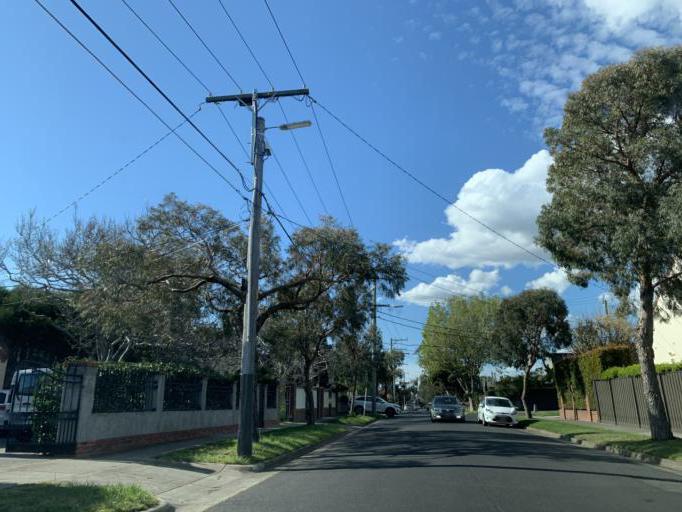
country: AU
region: Victoria
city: Hampton
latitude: -37.9556
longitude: 145.0124
